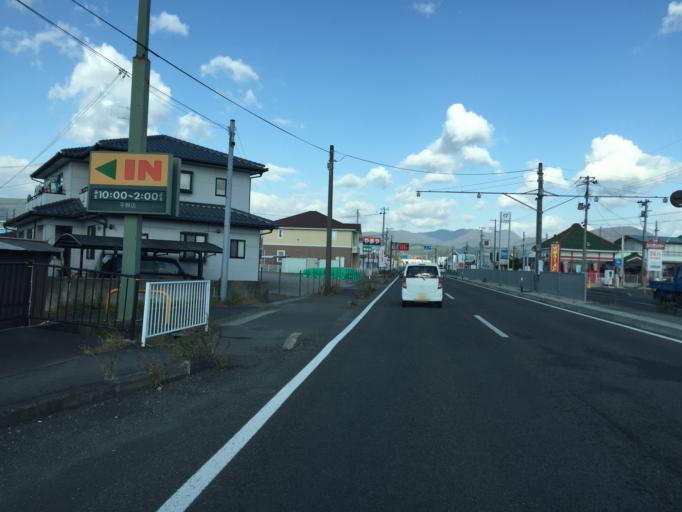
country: JP
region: Fukushima
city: Fukushima-shi
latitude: 37.8077
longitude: 140.4484
